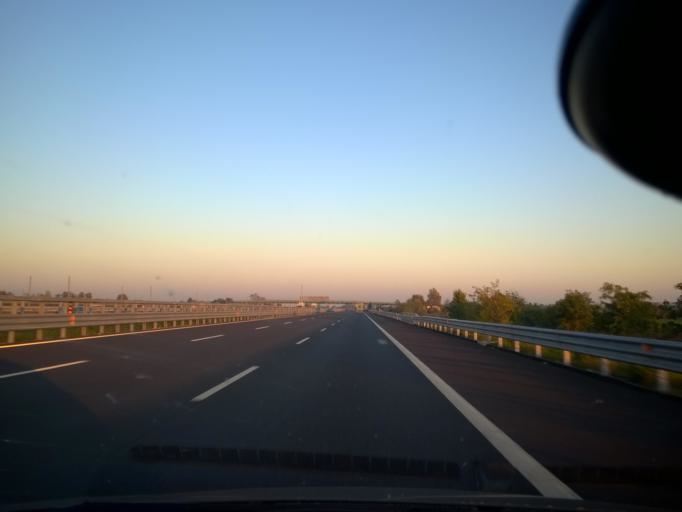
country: IT
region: Lombardy
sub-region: Provincia di Bergamo
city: Casirate d'Adda
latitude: 45.5049
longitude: 9.5728
